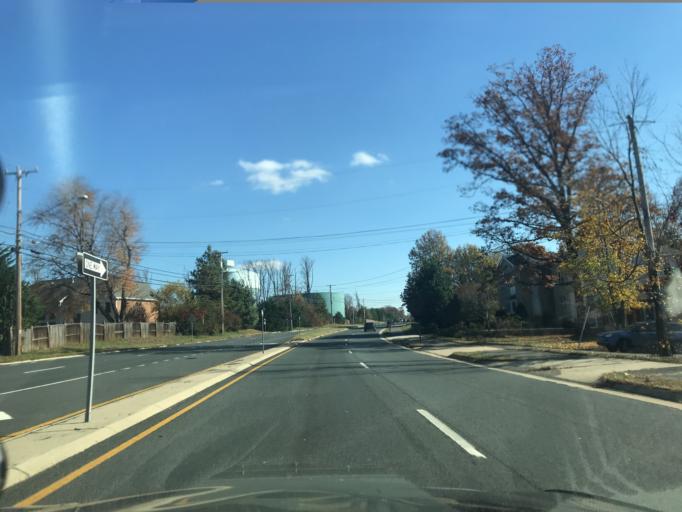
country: US
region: Virginia
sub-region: Fairfax County
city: Greenbriar
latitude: 38.8837
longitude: -77.3735
